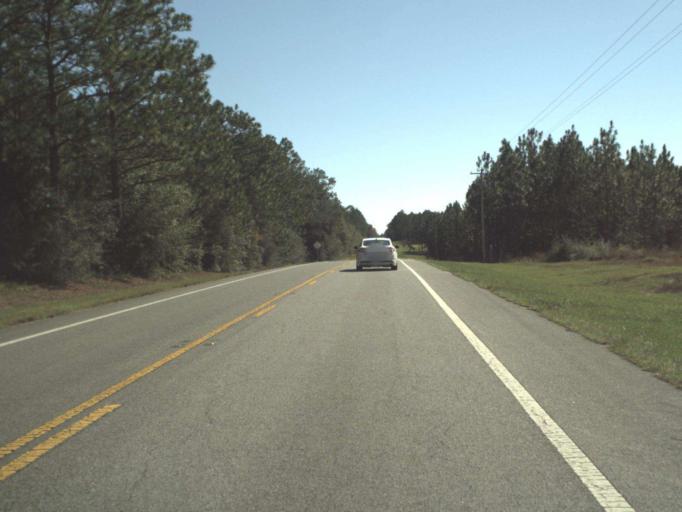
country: US
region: Florida
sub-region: Okaloosa County
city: Crestview
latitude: 30.8283
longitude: -86.7280
